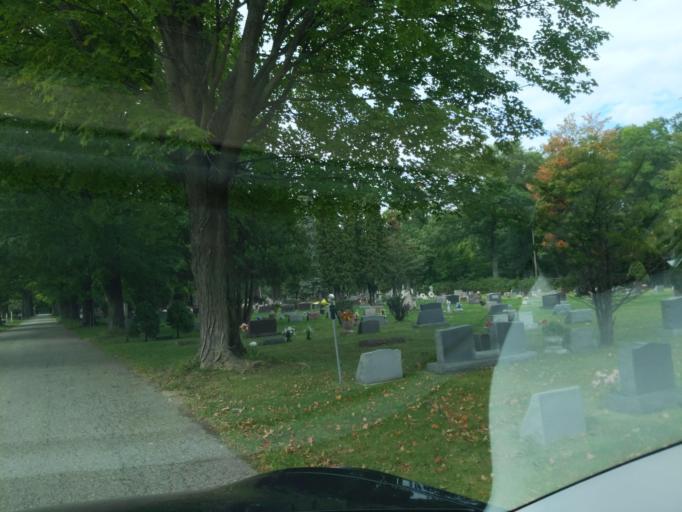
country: US
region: Michigan
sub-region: Grand Traverse County
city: Traverse City
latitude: 44.7544
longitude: -85.5841
